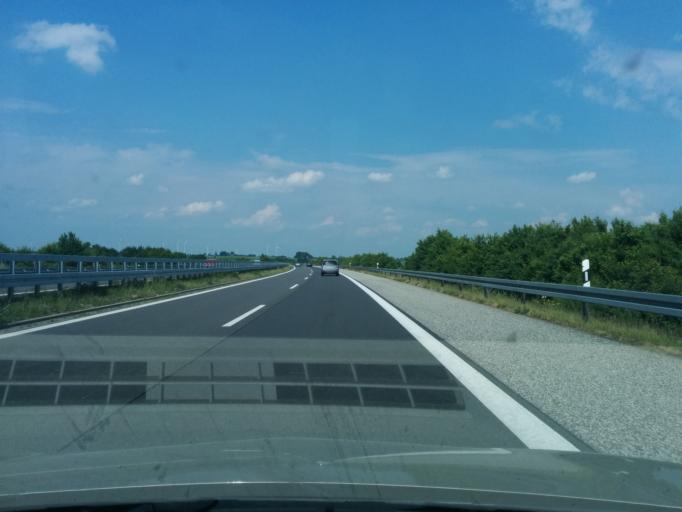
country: DE
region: Brandenburg
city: Grunow
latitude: 53.2842
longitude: 13.9893
